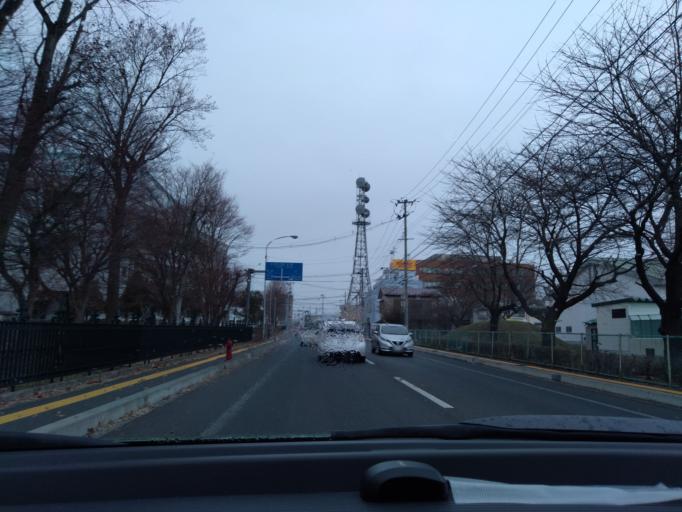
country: JP
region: Iwate
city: Morioka-shi
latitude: 39.7183
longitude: 141.1377
